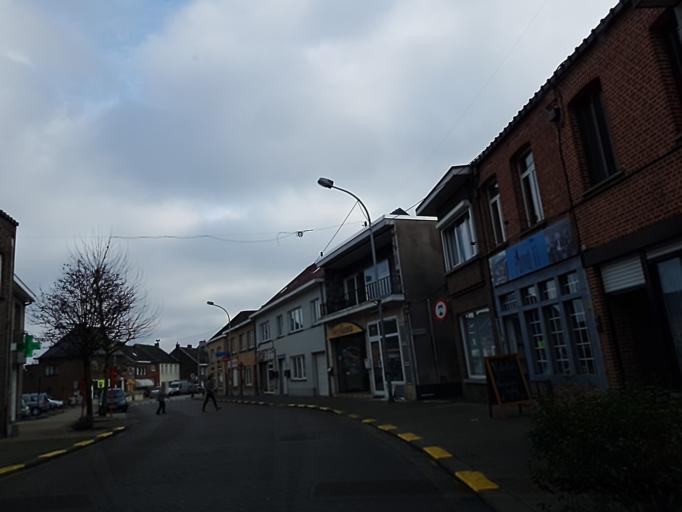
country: BE
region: Flanders
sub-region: Provincie Antwerpen
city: Putte
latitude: 51.0575
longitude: 4.6696
